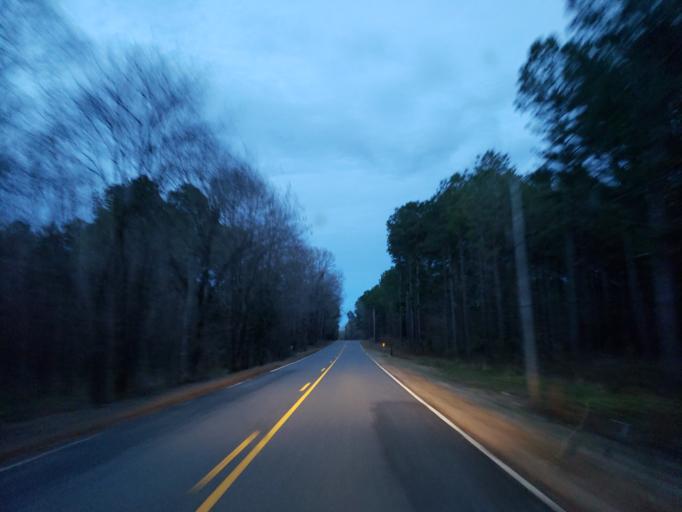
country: US
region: Alabama
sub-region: Greene County
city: Eutaw
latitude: 32.8840
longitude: -88.0593
